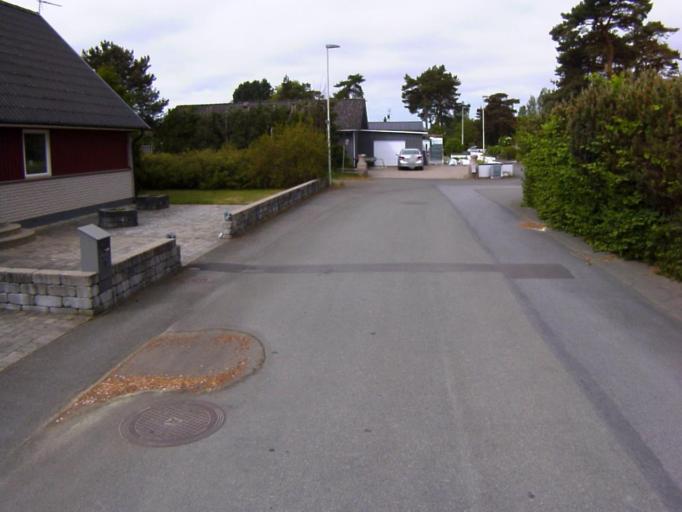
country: SE
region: Skane
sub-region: Kristianstads Kommun
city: Ahus
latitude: 55.9347
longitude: 14.2946
